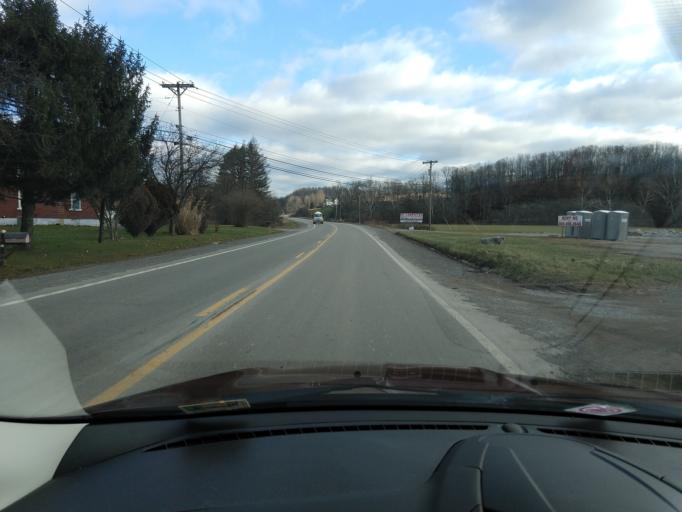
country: US
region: West Virginia
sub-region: Randolph County
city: Elkins
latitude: 38.8068
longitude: -79.8848
